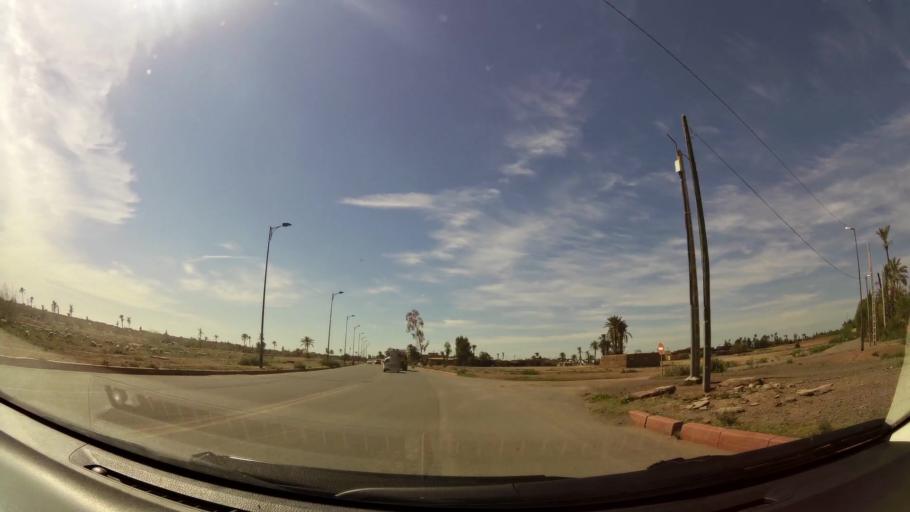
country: MA
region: Marrakech-Tensift-Al Haouz
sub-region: Marrakech
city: Marrakesh
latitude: 31.6184
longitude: -7.9577
